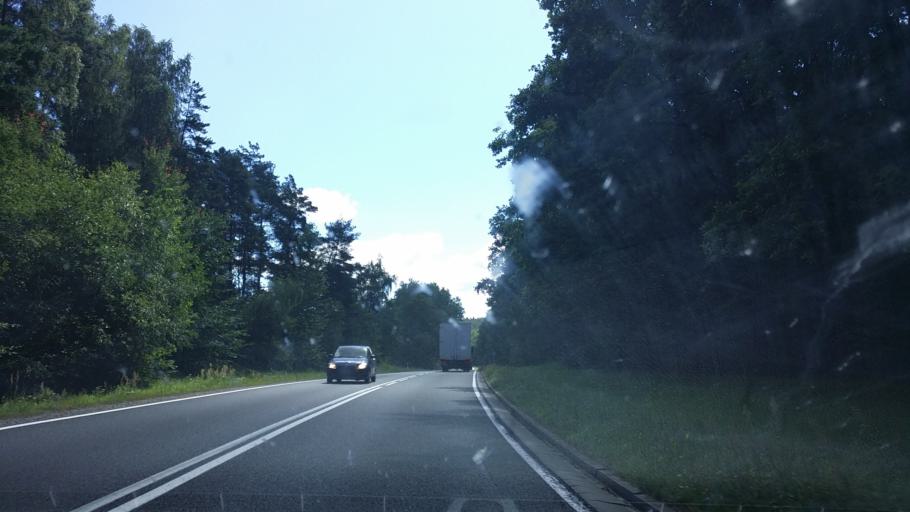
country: PL
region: West Pomeranian Voivodeship
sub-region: Powiat drawski
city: Kalisz Pomorski
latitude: 53.2951
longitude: 15.8515
